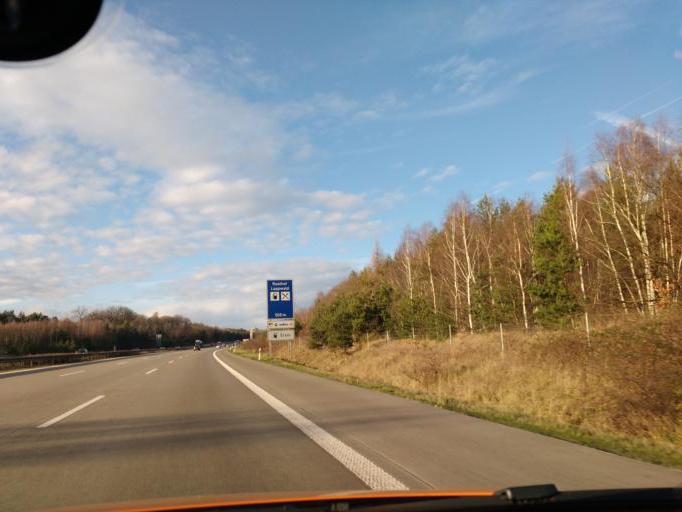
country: DE
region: Saxony-Anhalt
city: Beendorf
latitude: 52.2172
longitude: 11.0699
